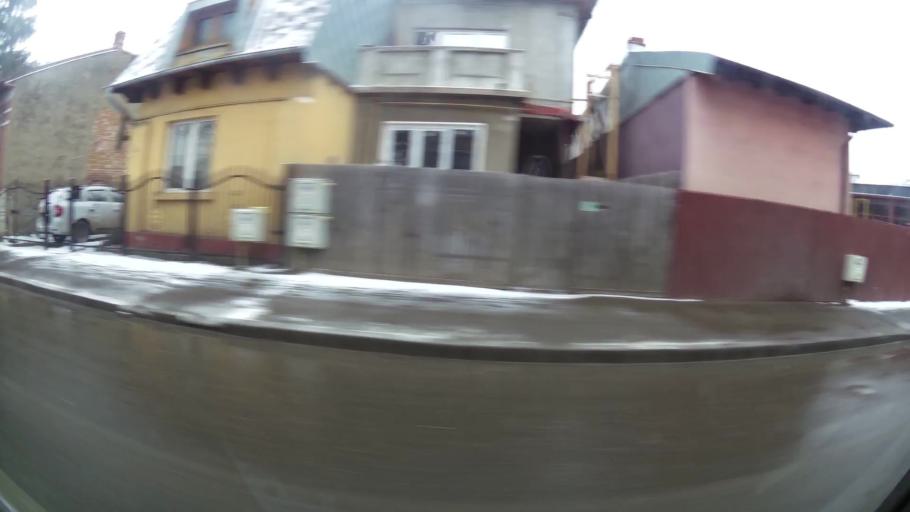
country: RO
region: Prahova
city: Ploiesti
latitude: 44.9345
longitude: 26.0359
